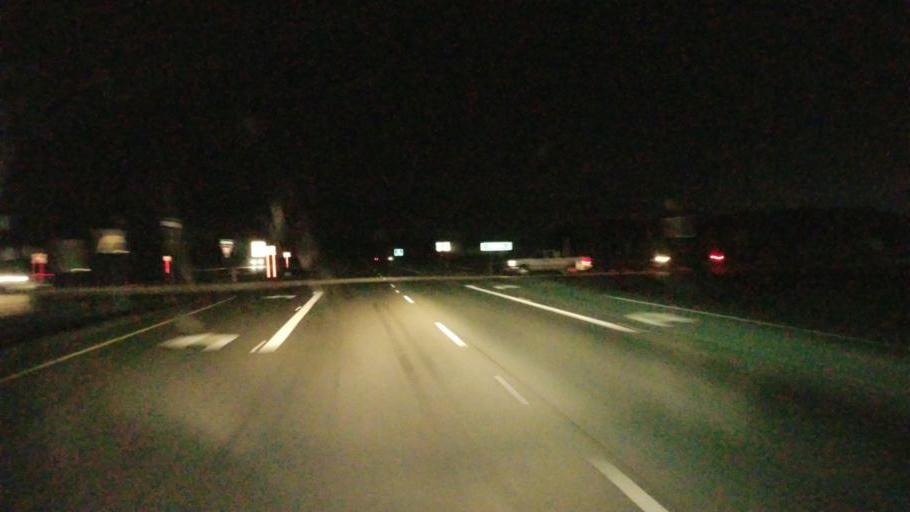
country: US
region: Ohio
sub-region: Wayne County
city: Wooster
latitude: 40.7929
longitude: -81.9821
